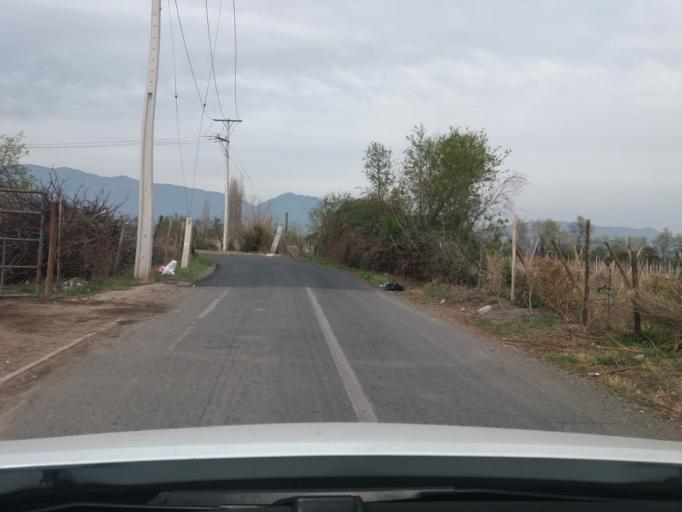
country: CL
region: Valparaiso
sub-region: Provincia de Los Andes
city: Los Andes
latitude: -32.8272
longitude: -70.6371
